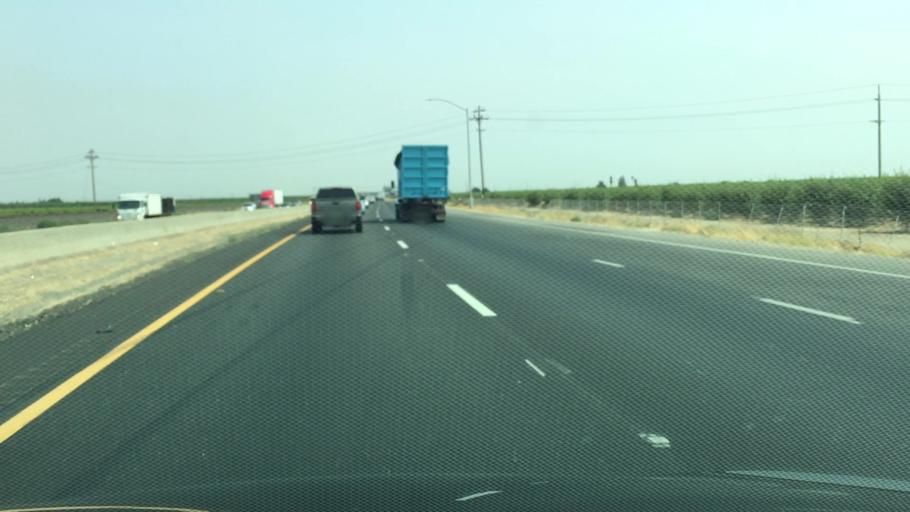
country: US
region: California
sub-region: Madera County
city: Parksdale
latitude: 36.9195
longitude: -120.0167
